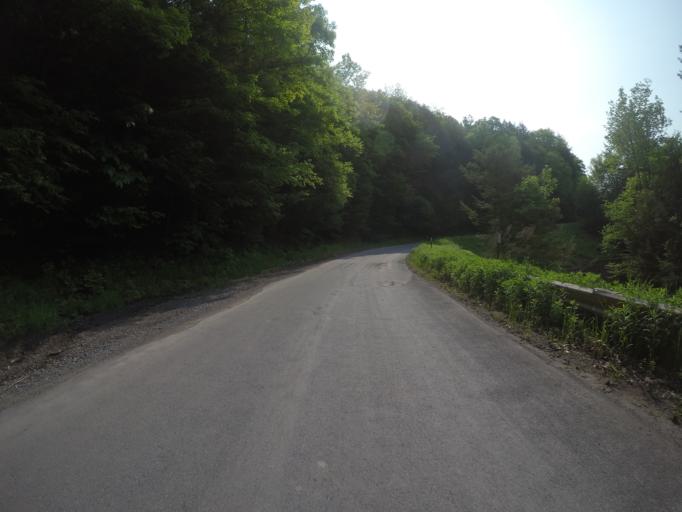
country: US
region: New York
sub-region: Sullivan County
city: Livingston Manor
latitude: 42.0761
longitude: -74.7654
